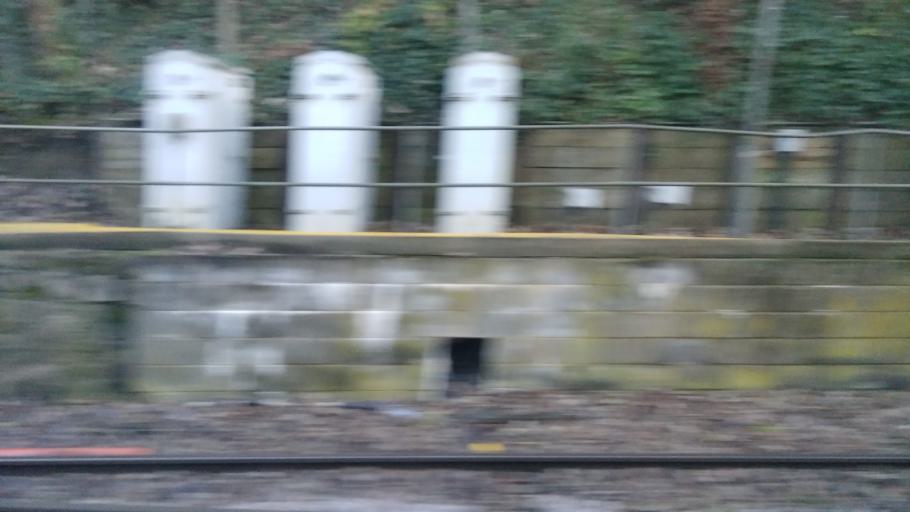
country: GB
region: England
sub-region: Kent
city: Sevenoaks
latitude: 51.2748
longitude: 0.1827
